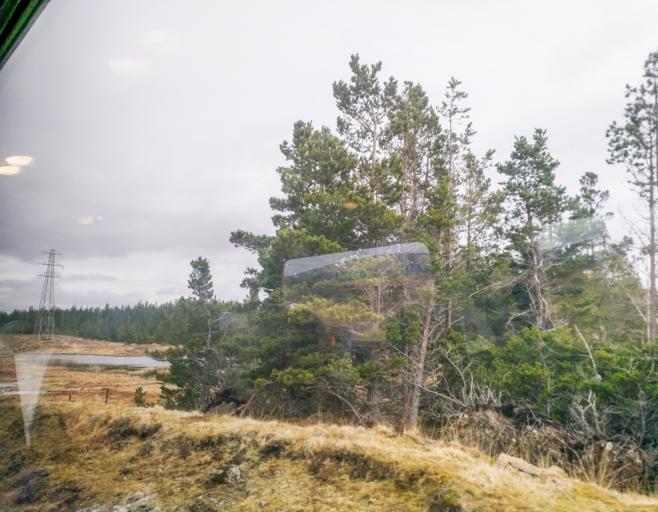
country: GB
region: Scotland
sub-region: Highland
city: Spean Bridge
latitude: 56.6555
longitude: -4.5651
